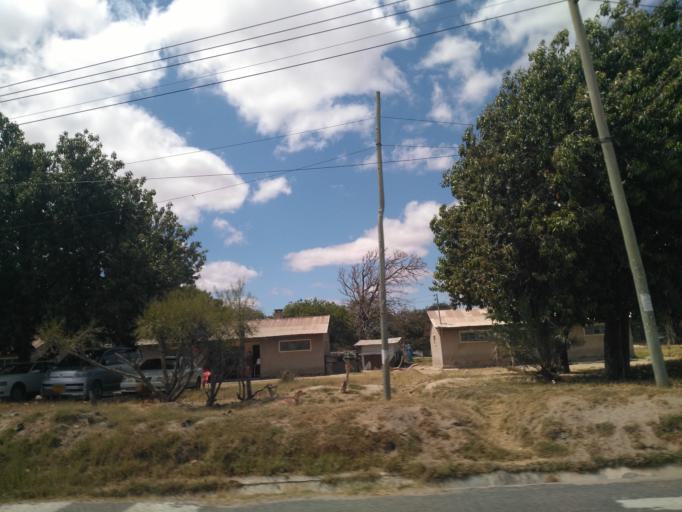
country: TZ
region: Dodoma
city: Dodoma
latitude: -6.1841
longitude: 35.7428
